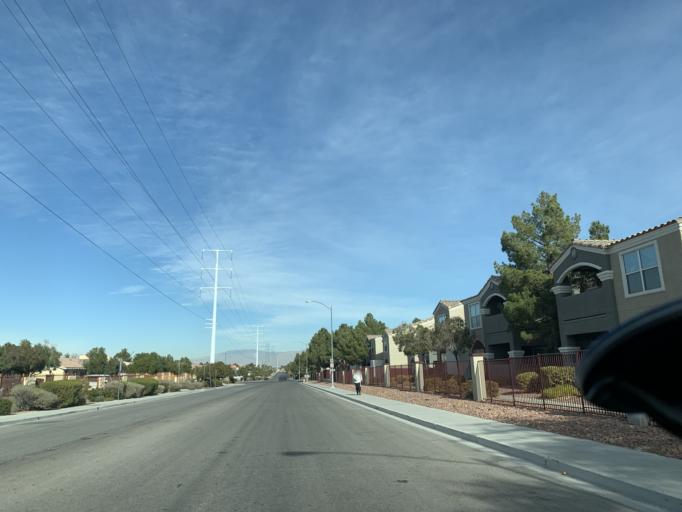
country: US
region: Nevada
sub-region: Clark County
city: Spring Valley
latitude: 36.0918
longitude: -115.2122
